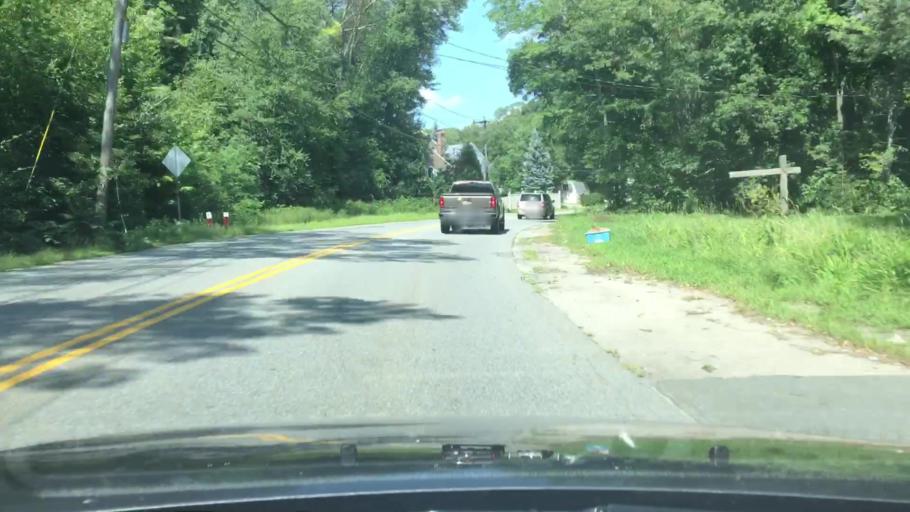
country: US
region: Massachusetts
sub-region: Worcester County
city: Milford
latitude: 42.1586
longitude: -71.5183
